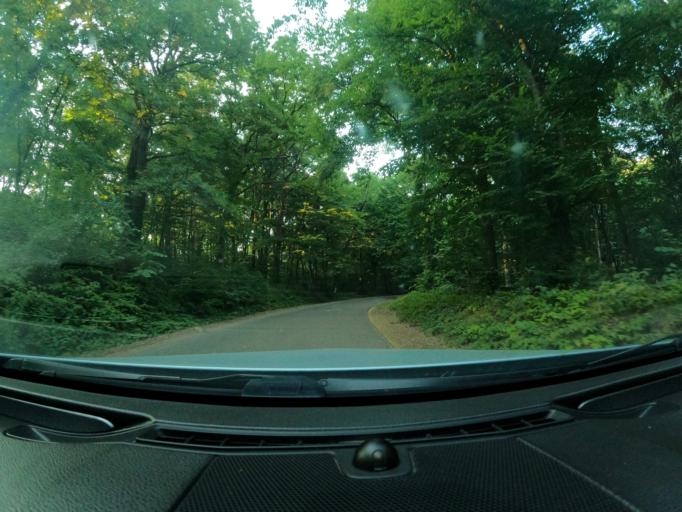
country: RS
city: Vrdnik
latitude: 45.1603
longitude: 19.7569
